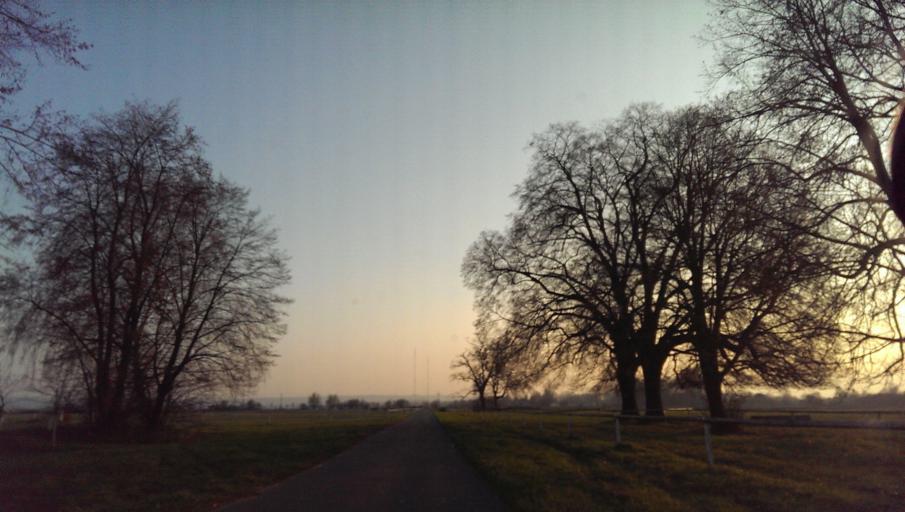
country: CZ
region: Zlin
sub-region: Okres Zlin
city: Napajedla
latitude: 49.1521
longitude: 17.5144
